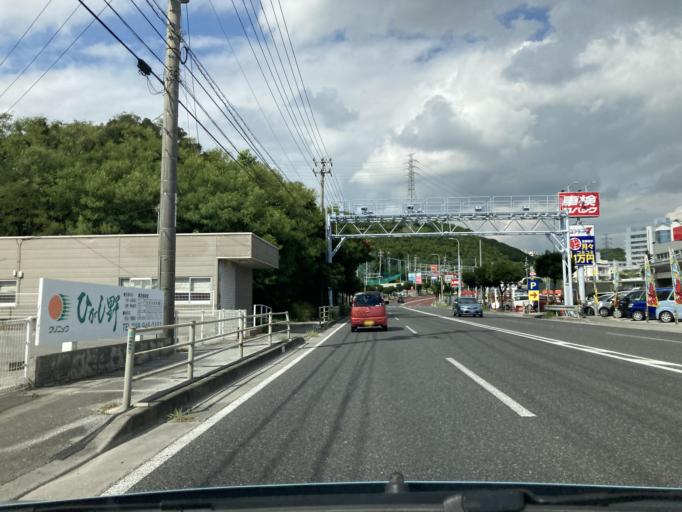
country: JP
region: Okinawa
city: Ginowan
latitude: 26.2343
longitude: 127.7697
